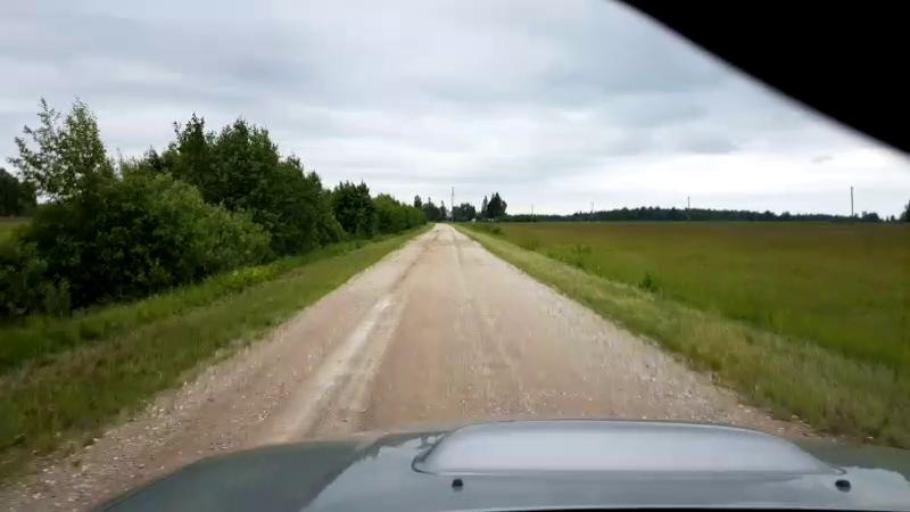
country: EE
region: Paernumaa
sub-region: Halinga vald
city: Parnu-Jaagupi
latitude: 58.5433
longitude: 24.5589
